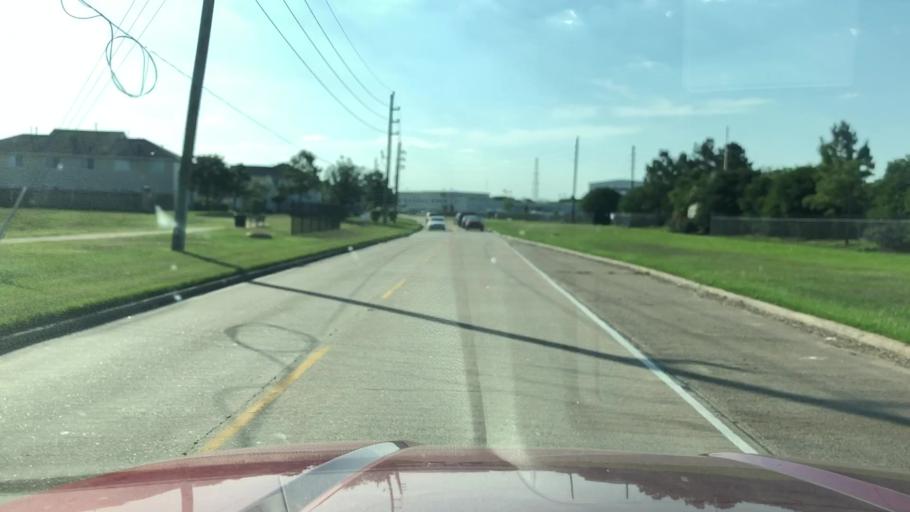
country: US
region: Texas
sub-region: Harris County
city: Hudson
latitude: 29.9448
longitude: -95.4933
